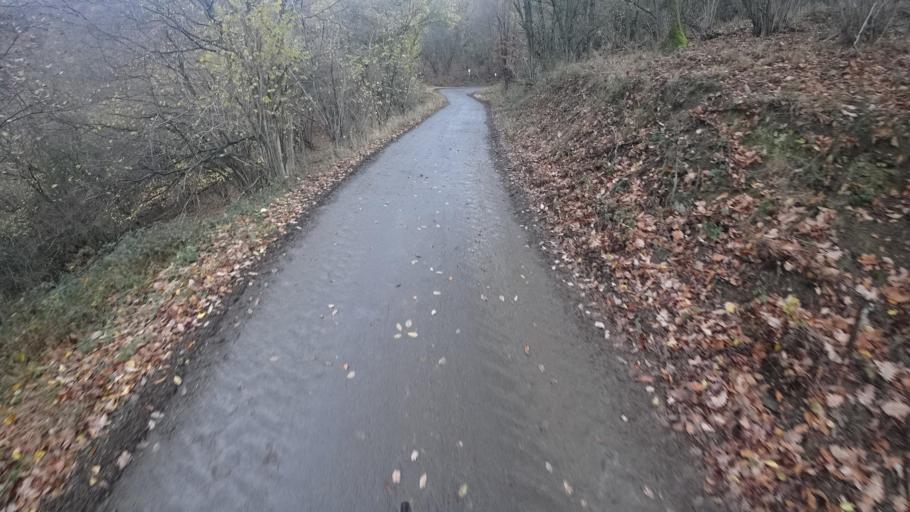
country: DE
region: Rheinland-Pfalz
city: Kesseling
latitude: 50.4926
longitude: 7.0145
